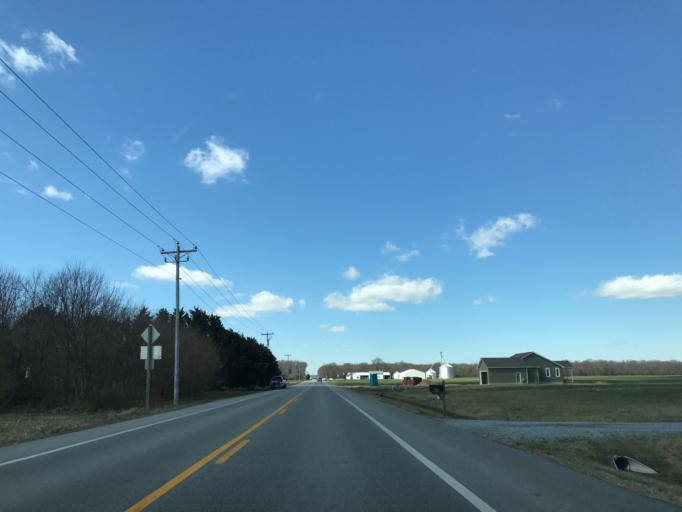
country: US
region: Maryland
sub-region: Caroline County
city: Greensboro
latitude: 39.0932
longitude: -75.8786
